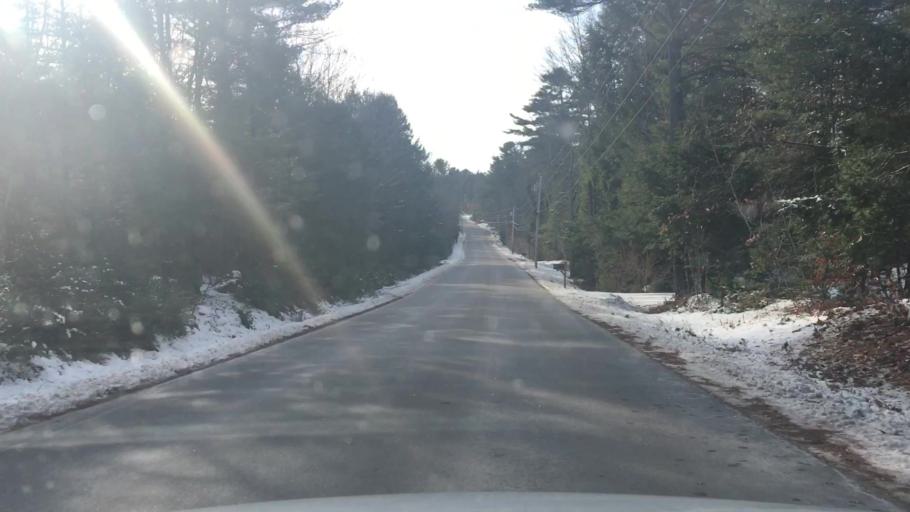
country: US
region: Maine
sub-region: Cumberland County
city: Freeport
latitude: 43.8909
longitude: -70.0847
